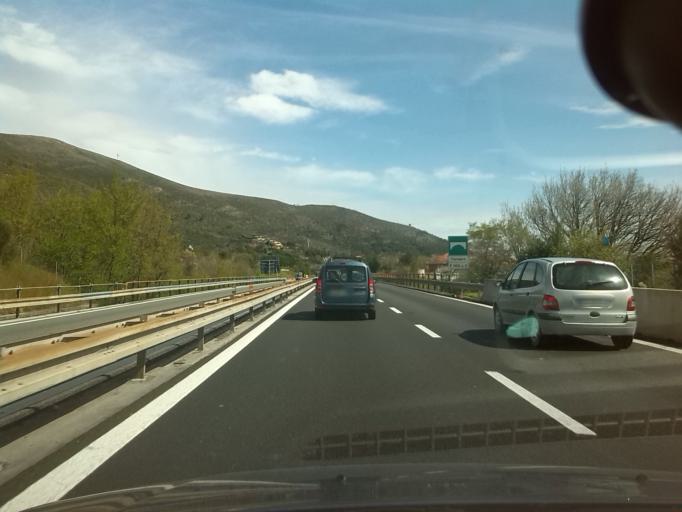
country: IT
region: Liguria
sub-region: Provincia di Savona
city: Ceriale
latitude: 44.0915
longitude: 8.2108
